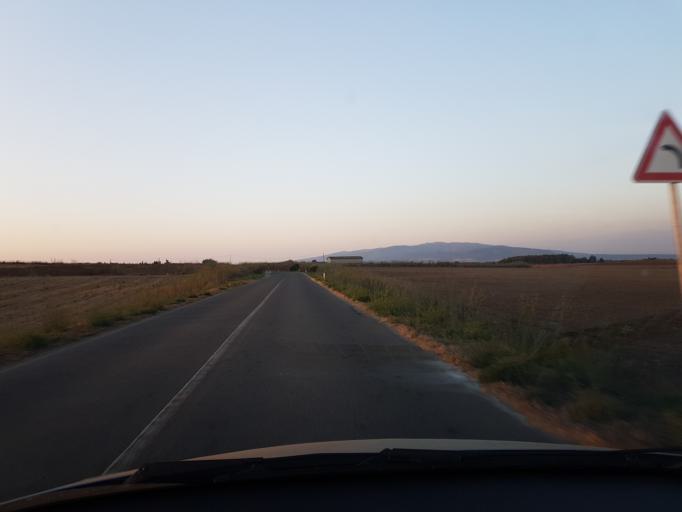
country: IT
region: Sardinia
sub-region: Provincia di Oristano
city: Nurachi
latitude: 39.9763
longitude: 8.4536
